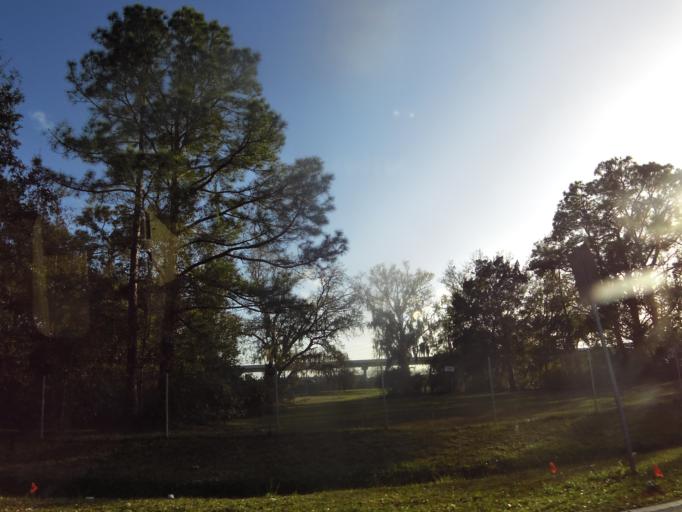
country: US
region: Florida
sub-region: Duval County
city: Jacksonville
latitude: 30.2517
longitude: -81.5937
